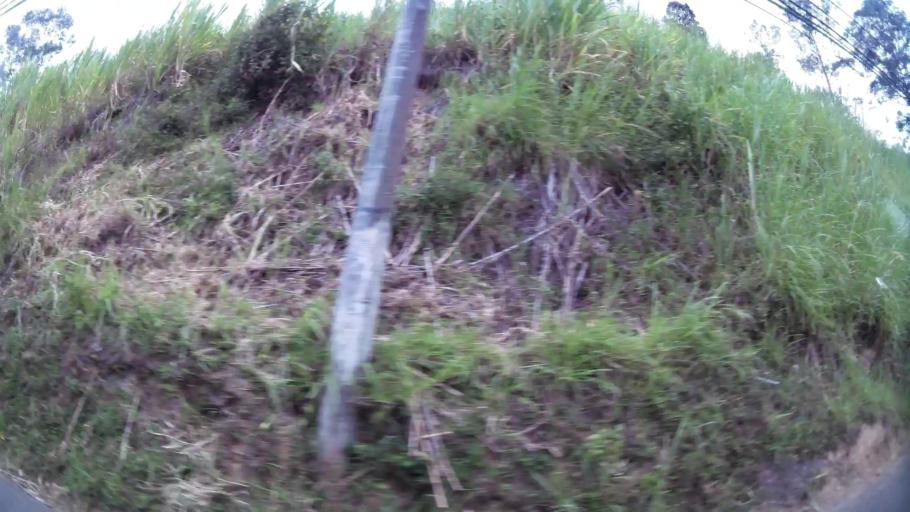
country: CO
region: Antioquia
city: Municipio de Copacabana
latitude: 6.3377
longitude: -75.5034
